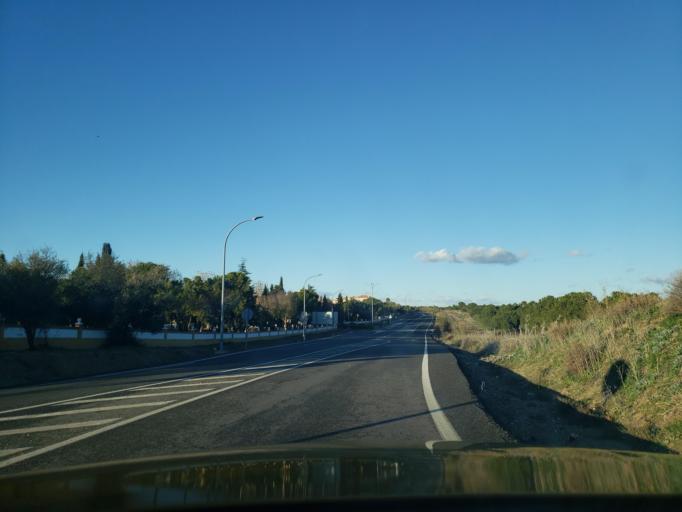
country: ES
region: Castille-La Mancha
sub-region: Province of Toledo
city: Cobisa
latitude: 39.8193
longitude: -4.0195
